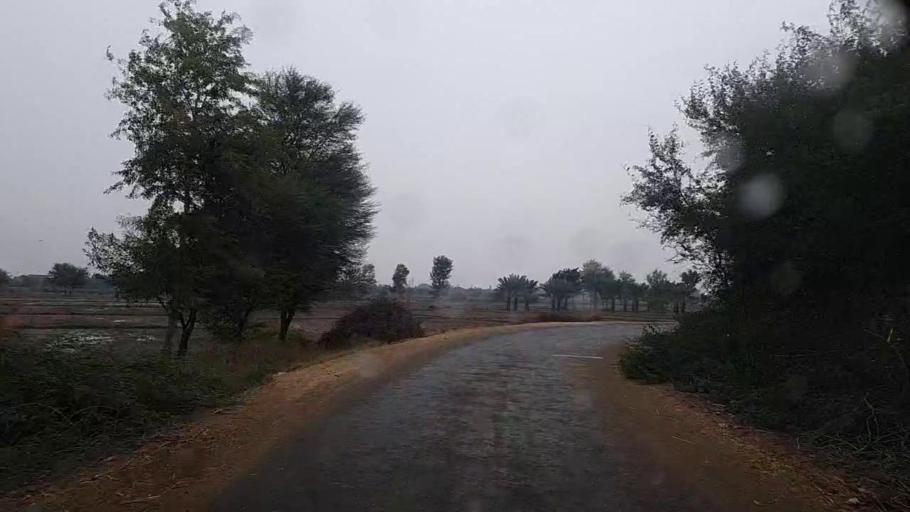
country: PK
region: Sindh
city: Ranipur
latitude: 27.2610
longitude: 68.5753
